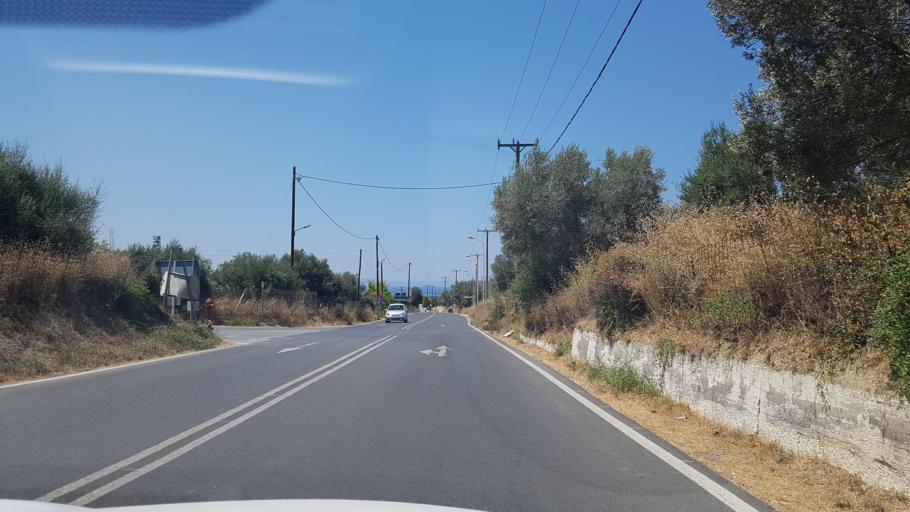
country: GR
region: Crete
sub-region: Nomos Rethymnis
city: Rethymno
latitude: 35.3578
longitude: 24.5546
